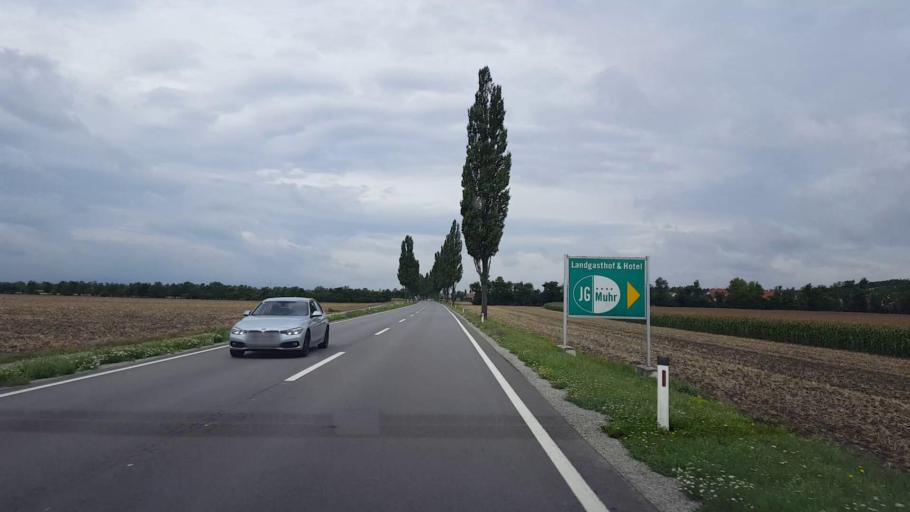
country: AT
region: Lower Austria
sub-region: Politischer Bezirk Bruck an der Leitha
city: Trautmannsdorf an der Leitha
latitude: 48.0486
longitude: 16.6517
